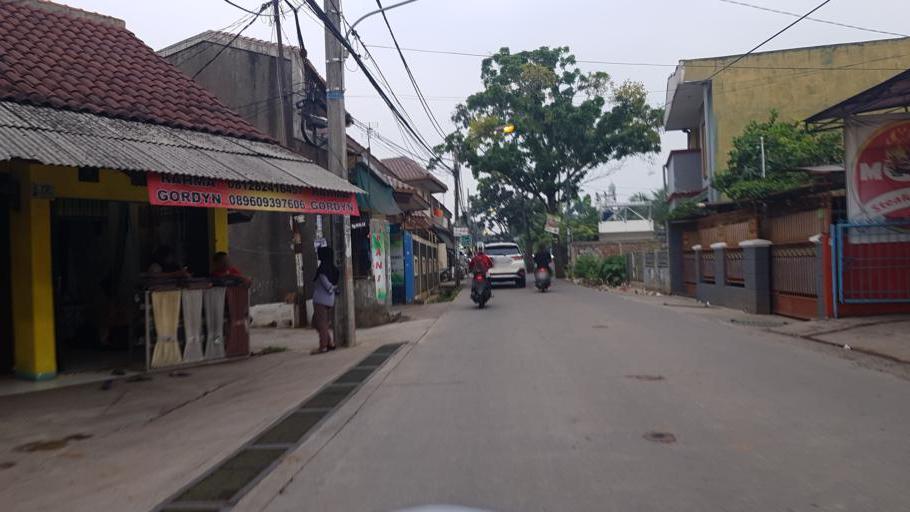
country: ID
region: West Java
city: Depok
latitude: -6.3700
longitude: 106.7996
